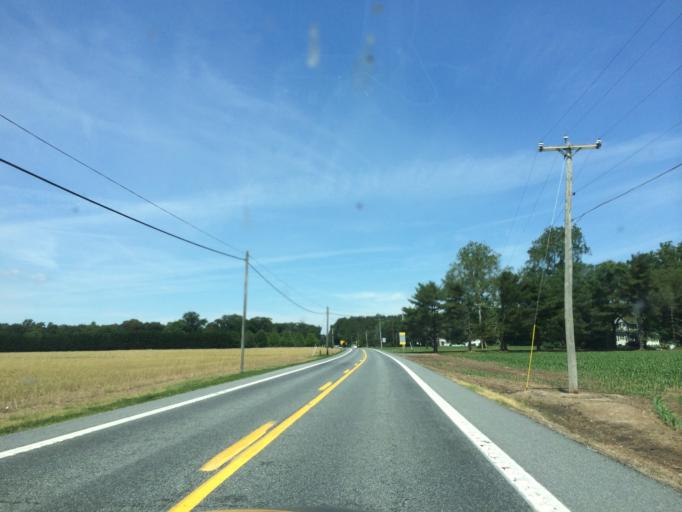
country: US
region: Maryland
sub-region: Wicomico County
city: Salisbury
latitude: 38.3192
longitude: -75.5460
